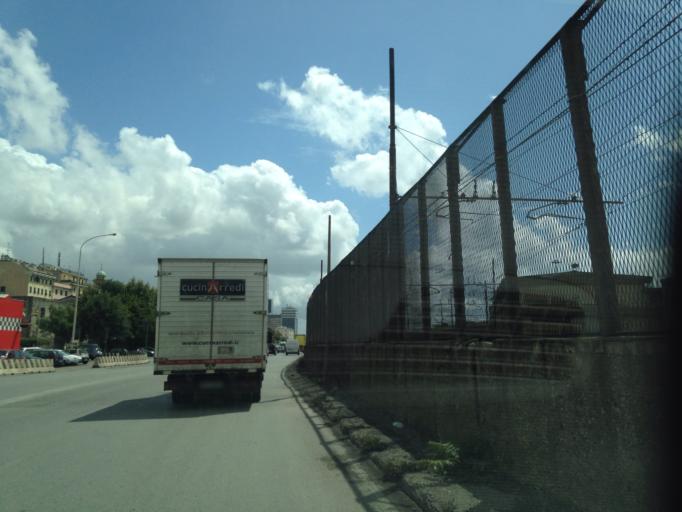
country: IT
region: Liguria
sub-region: Provincia di Genova
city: San Teodoro
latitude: 44.4099
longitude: 8.8872
